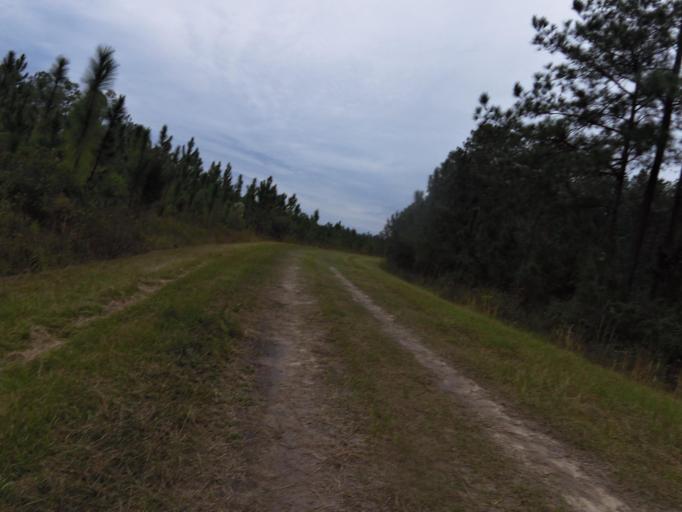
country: US
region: Florida
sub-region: Putnam County
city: Palatka
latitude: 29.6812
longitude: -81.7421
